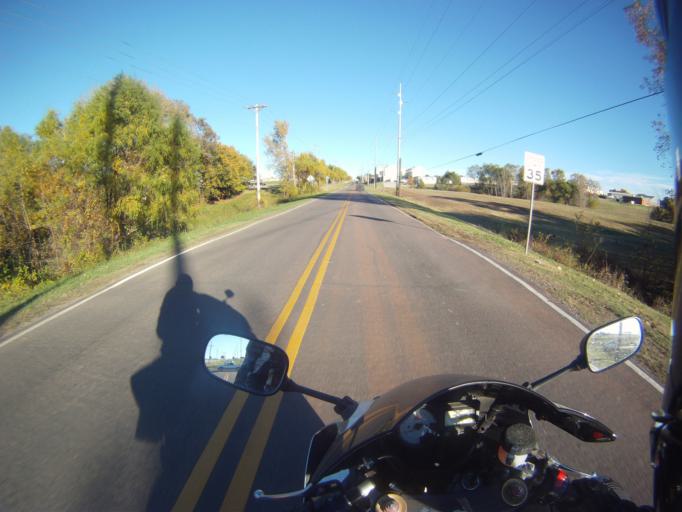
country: US
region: Oklahoma
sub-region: Payne County
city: Stillwater
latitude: 36.1303
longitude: -97.0870
